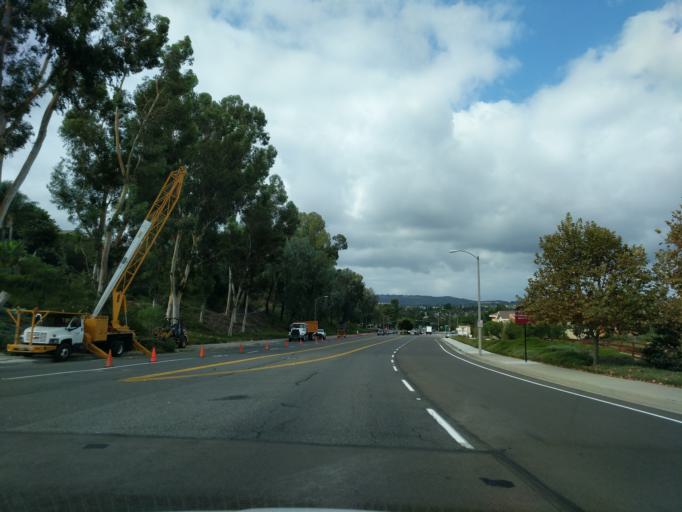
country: US
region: California
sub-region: Orange County
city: Aliso Viejo
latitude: 33.5773
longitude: -117.6991
